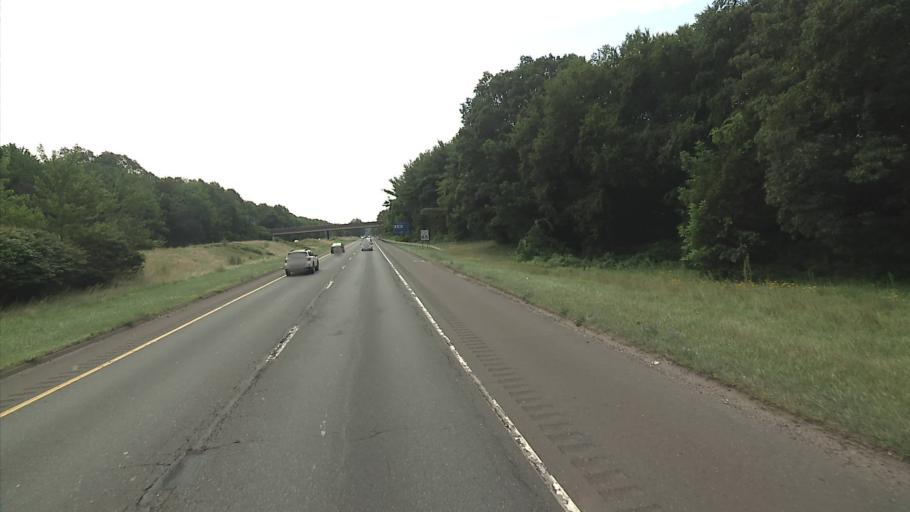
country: US
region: Connecticut
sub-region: Fairfield County
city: Newtown
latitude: 41.4242
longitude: -73.3027
